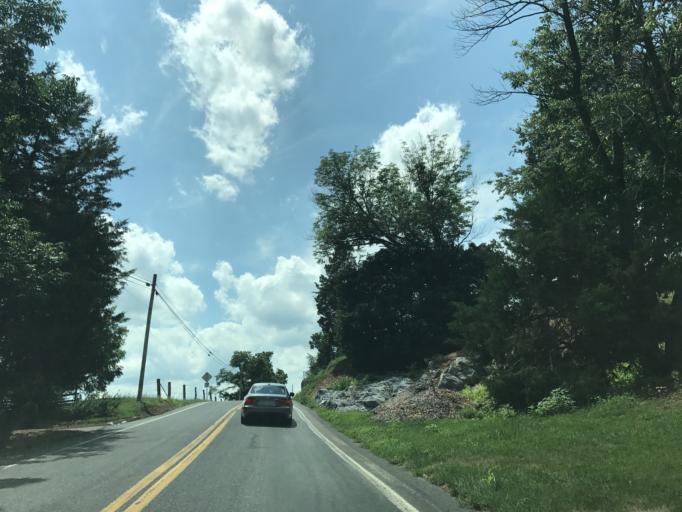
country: US
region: Pennsylvania
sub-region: Lancaster County
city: Clay
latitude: 40.2177
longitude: -76.2690
